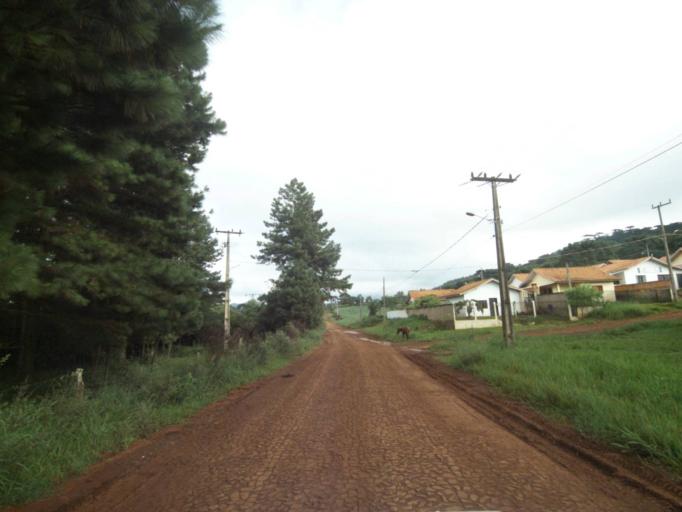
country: BR
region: Parana
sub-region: Pitanga
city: Pitanga
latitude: -24.9392
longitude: -51.8663
